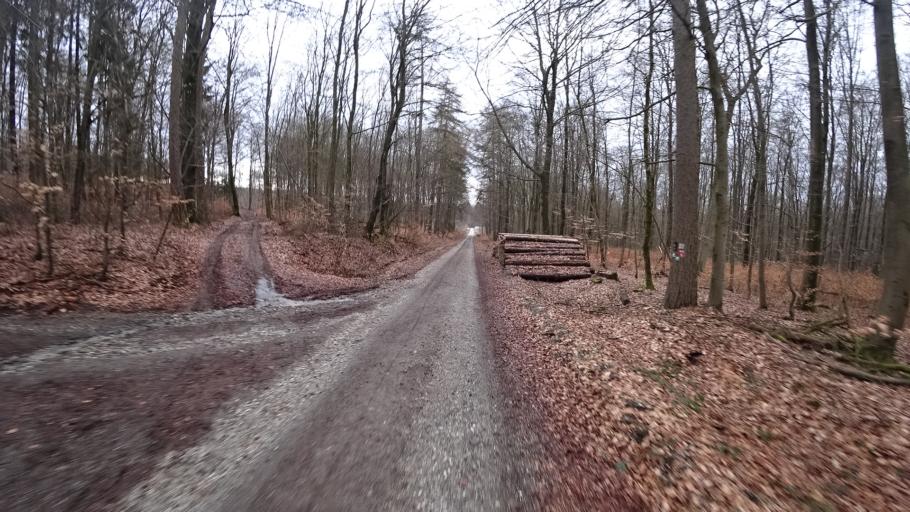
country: DE
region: Rheinland-Pfalz
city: Hundsdorf
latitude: 50.4396
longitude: 7.7097
